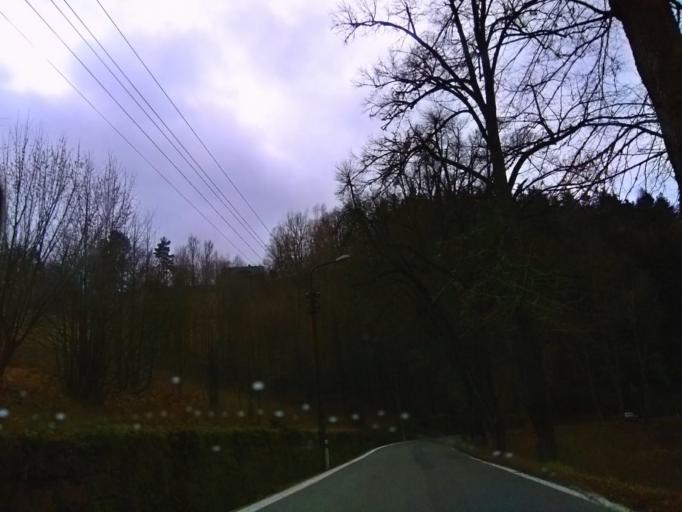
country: CZ
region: Jihocesky
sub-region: Okres Cesky Krumlov
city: Vyssi Brod
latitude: 48.6524
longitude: 14.3625
